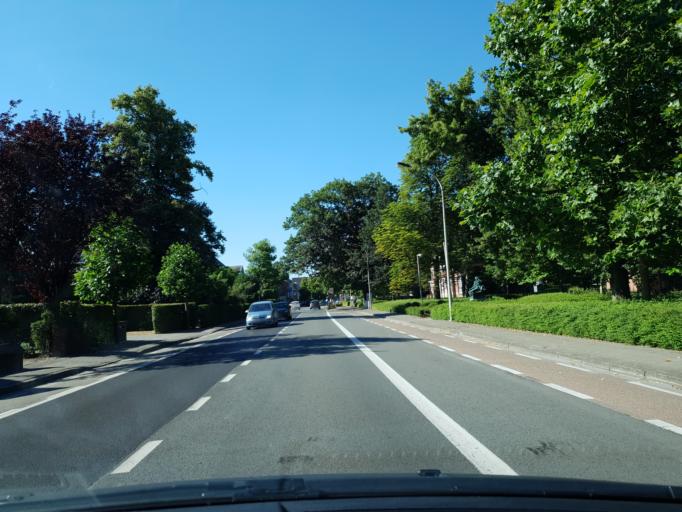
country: BE
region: Flanders
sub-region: Provincie Antwerpen
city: Beerse
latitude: 51.3172
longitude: 4.8558
